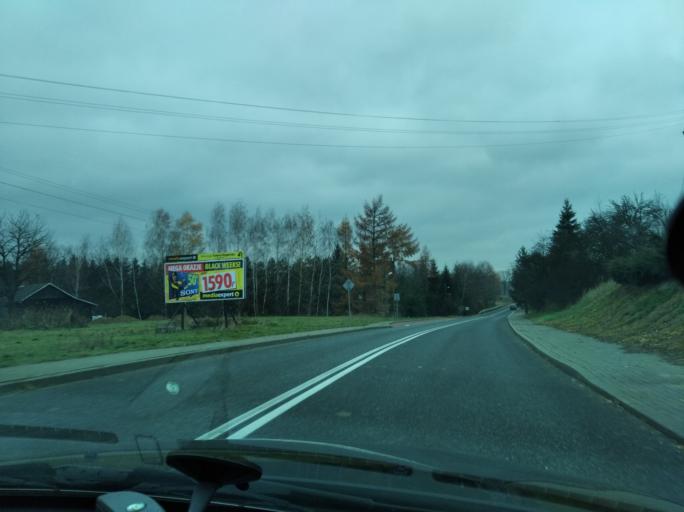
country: PL
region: Subcarpathian Voivodeship
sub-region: Powiat przeworski
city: Kanczuga
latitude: 49.9839
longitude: 22.4013
